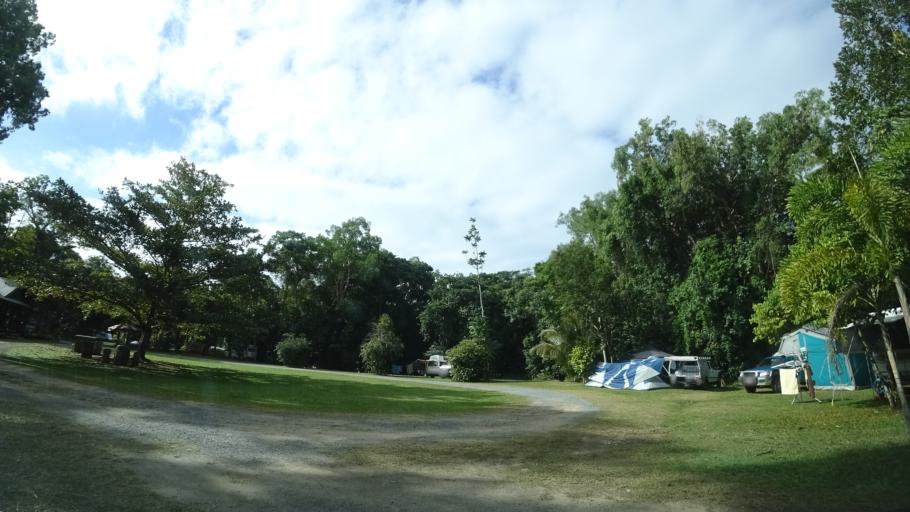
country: AU
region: Queensland
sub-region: Cairns
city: Port Douglas
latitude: -16.0966
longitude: 145.4647
